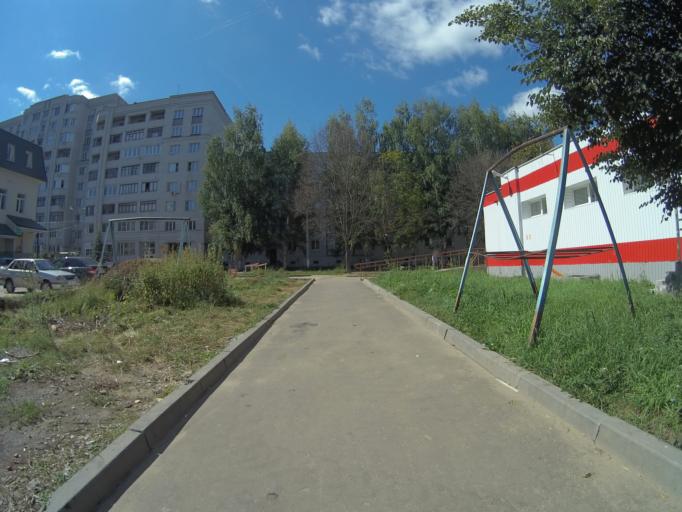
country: RU
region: Vladimir
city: Vladimir
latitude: 56.1323
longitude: 40.3714
